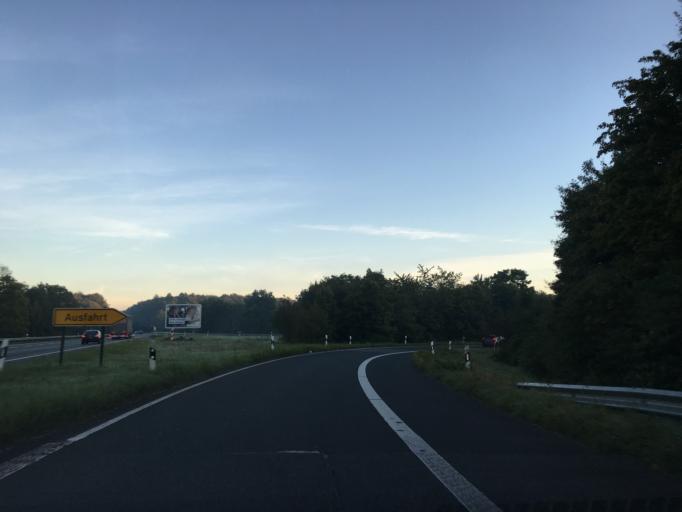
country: DE
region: North Rhine-Westphalia
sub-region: Regierungsbezirk Munster
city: Steinfurt
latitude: 52.1393
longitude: 7.3658
